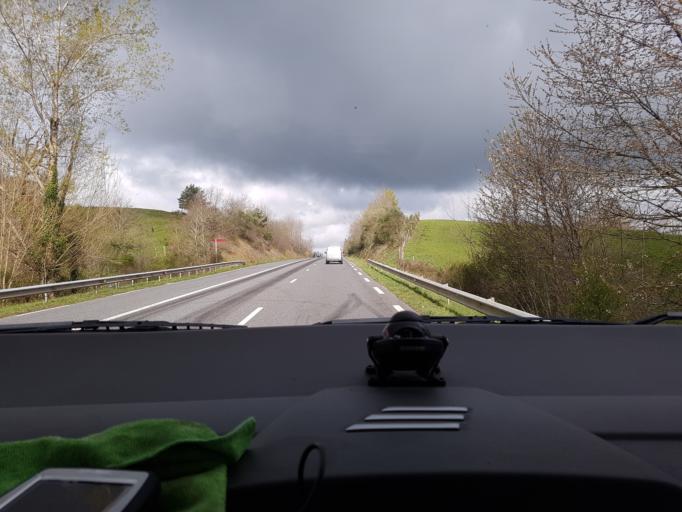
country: FR
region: Midi-Pyrenees
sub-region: Departement de l'Aveyron
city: Moyrazes
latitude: 44.3795
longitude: 2.4128
